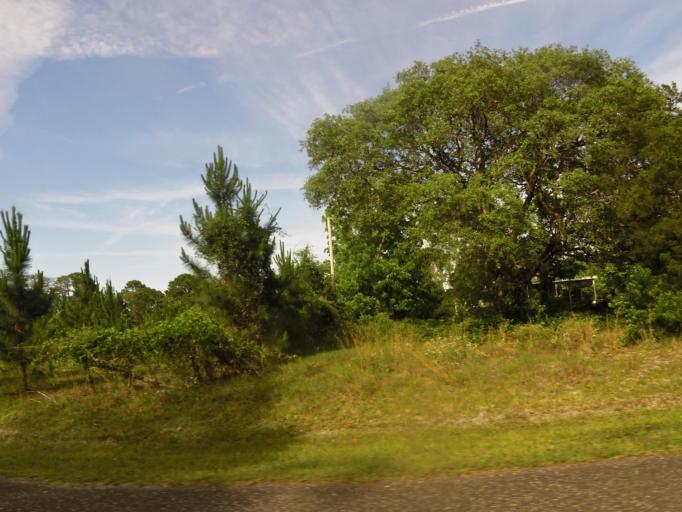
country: US
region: Florida
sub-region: Nassau County
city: Fernandina Beach
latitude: 30.5297
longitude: -81.4877
